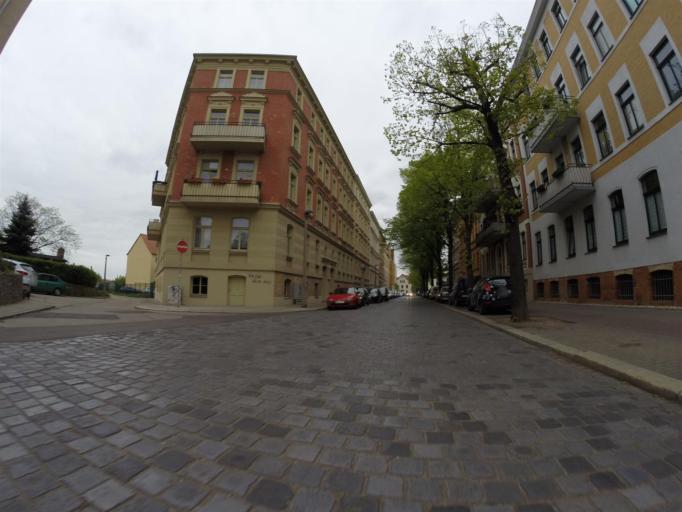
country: DE
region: Saxony-Anhalt
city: Halle (Saale)
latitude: 51.4701
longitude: 11.9682
